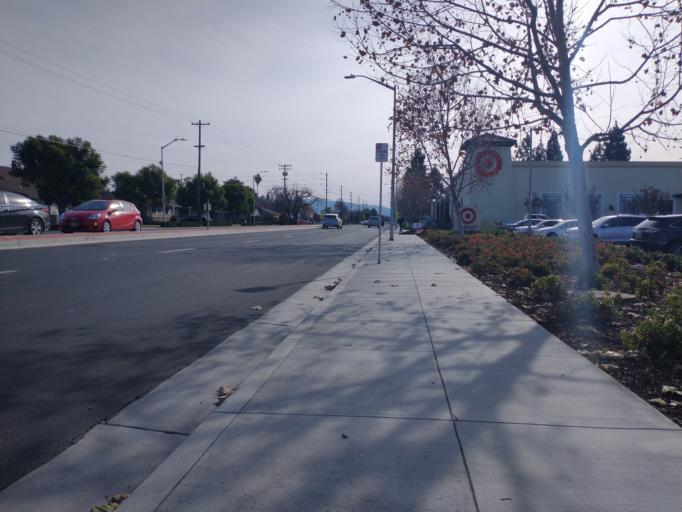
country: US
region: California
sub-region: Santa Clara County
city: Santa Clara
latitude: 37.3509
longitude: -121.9596
